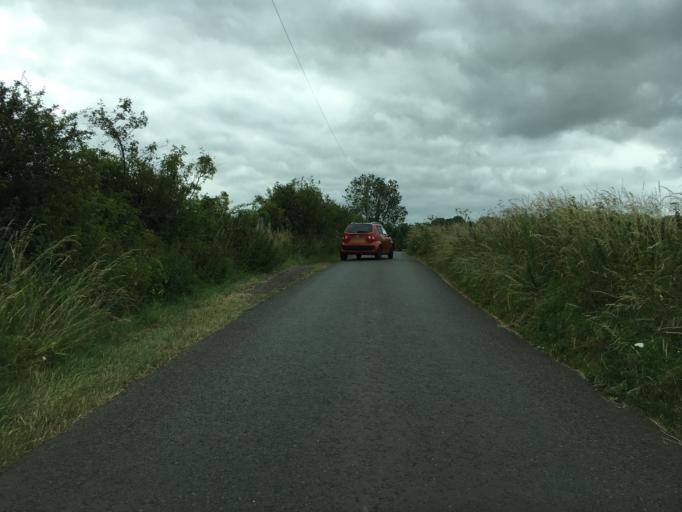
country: GB
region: England
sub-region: Gloucestershire
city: Shipton Village
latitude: 51.8910
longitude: -1.9132
